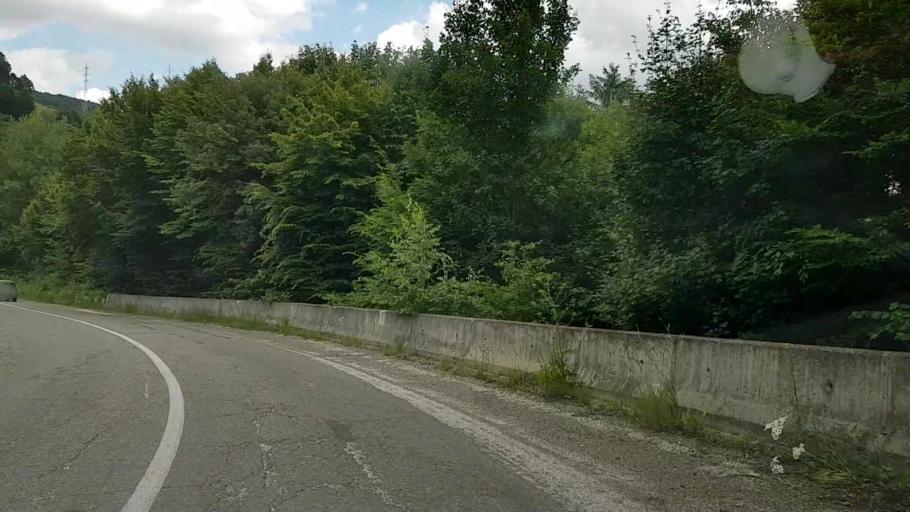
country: RO
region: Neamt
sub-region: Comuna Pangarati
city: Pangarati
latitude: 46.9548
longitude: 26.1228
